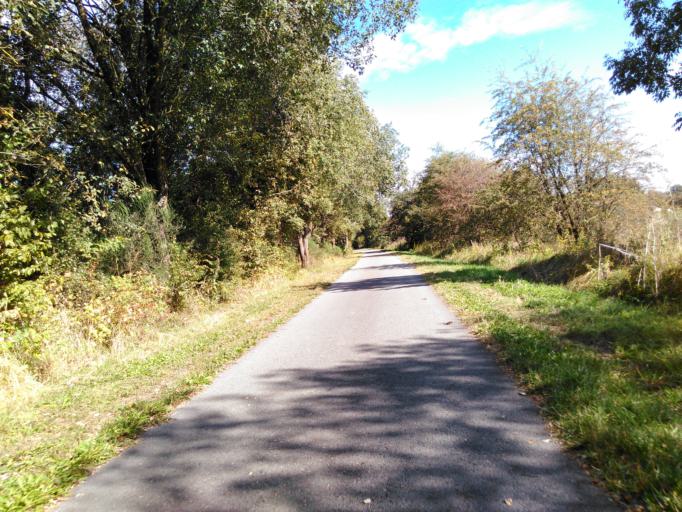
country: BE
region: Wallonia
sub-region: Province du Luxembourg
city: Bastogne
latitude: 50.0111
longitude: 5.7341
